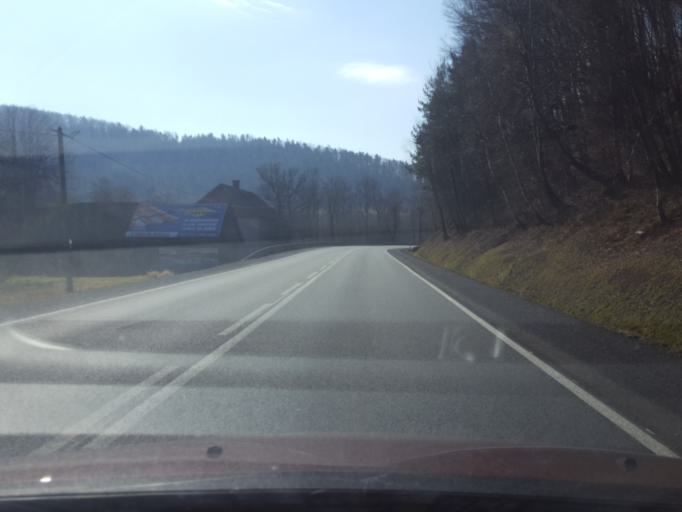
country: PL
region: Lesser Poland Voivodeship
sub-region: Powiat nowosadecki
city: Lososina Dolna
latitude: 49.7738
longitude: 20.6429
